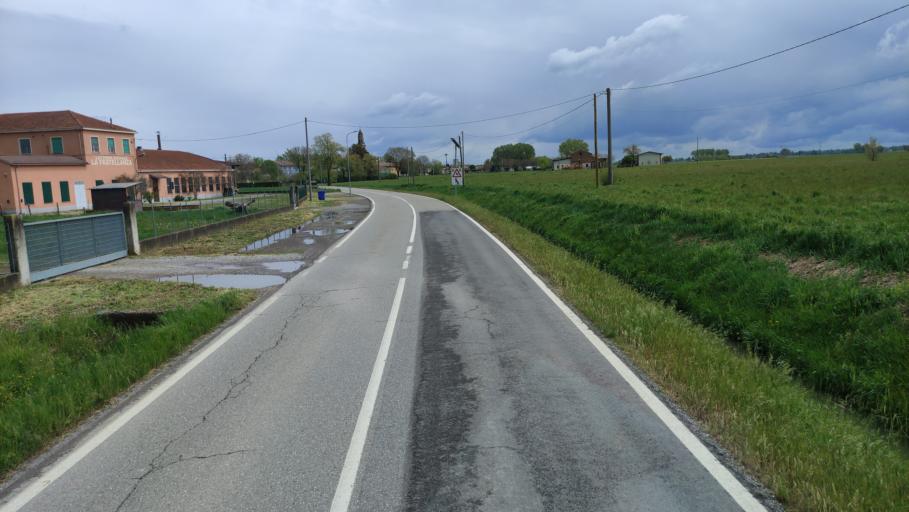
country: IT
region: Emilia-Romagna
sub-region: Provincia di Parma
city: Trecasali
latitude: 44.9533
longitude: 10.2892
